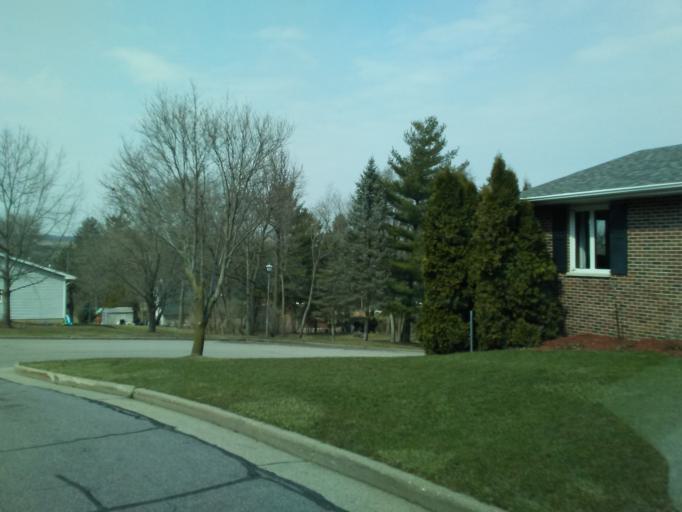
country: US
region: Wisconsin
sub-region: Columbia County
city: Lodi
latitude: 43.3071
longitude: -89.5238
